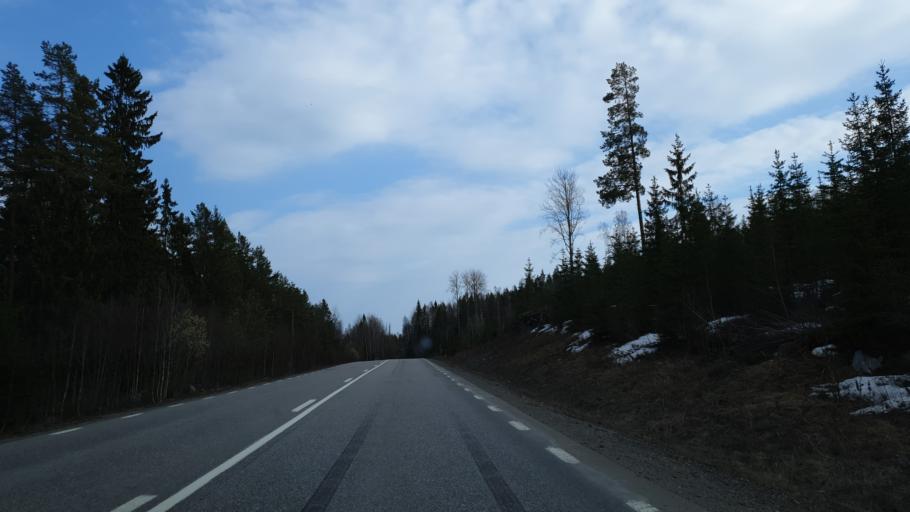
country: SE
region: Gaevleborg
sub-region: Hudiksvalls Kommun
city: Iggesund
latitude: 61.6523
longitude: 17.0280
